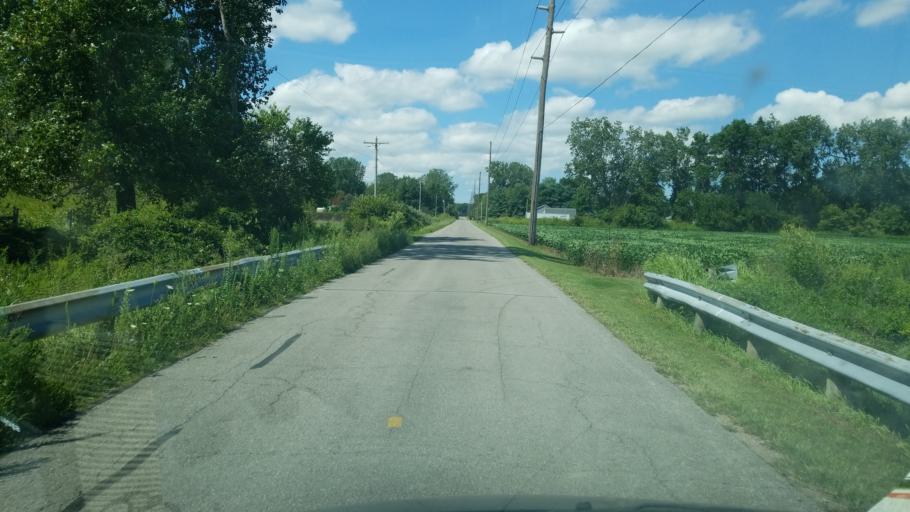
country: US
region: Ohio
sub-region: Henry County
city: Liberty Center
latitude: 41.4512
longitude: -83.9065
